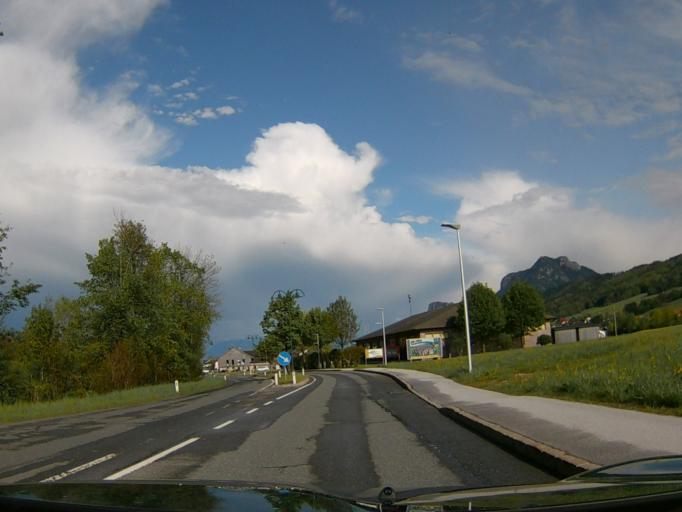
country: AT
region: Salzburg
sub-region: Politischer Bezirk Salzburg-Umgebung
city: Thalgau
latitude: 47.8410
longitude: 13.2428
